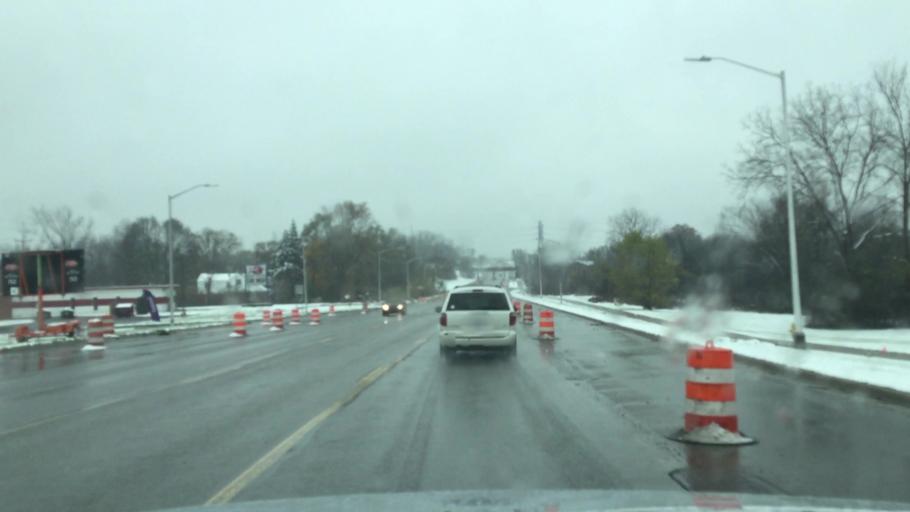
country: US
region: Michigan
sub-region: Oakland County
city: Auburn Hills
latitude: 42.6707
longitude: -83.2555
